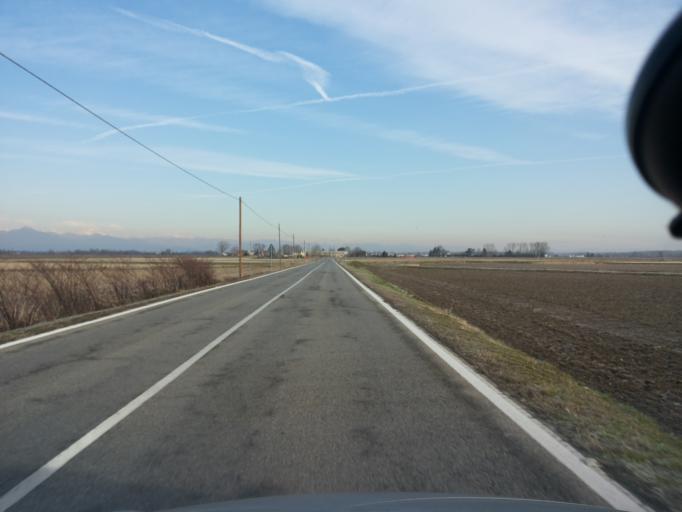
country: IT
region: Piedmont
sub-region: Provincia di Vercelli
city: Quinto Vercellese
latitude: 45.3846
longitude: 8.3761
